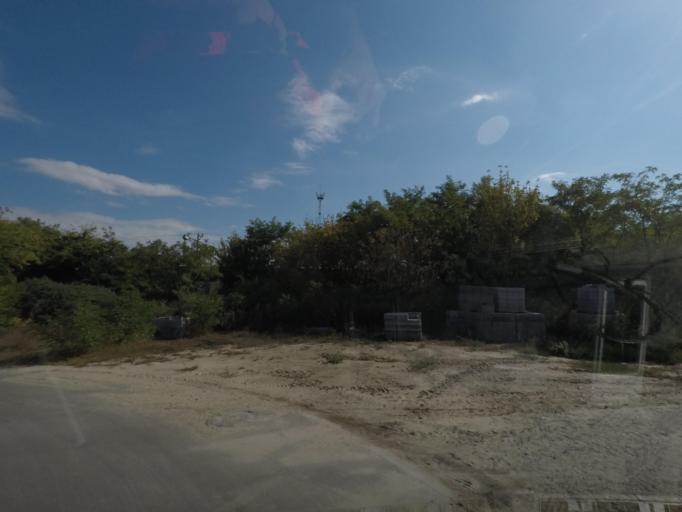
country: HU
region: Budapest
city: Budapest XXIII. keruelet
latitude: 47.3812
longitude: 19.1177
